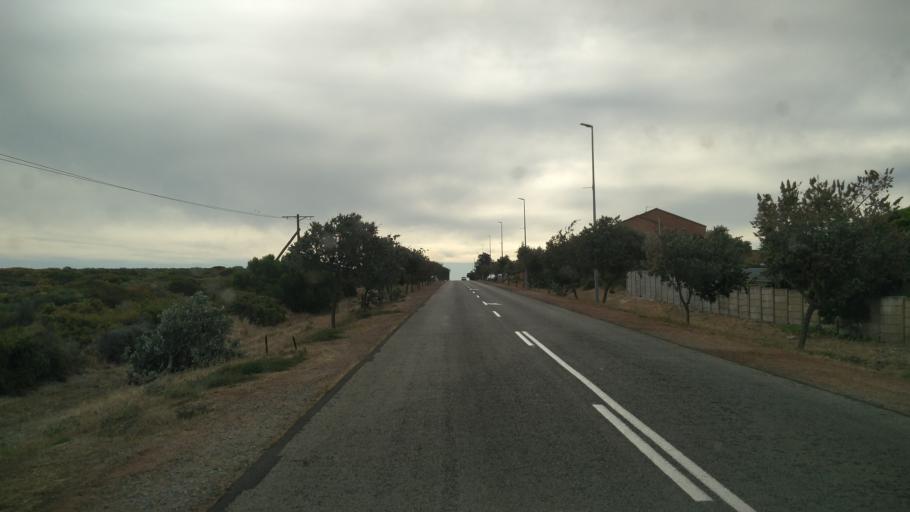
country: ZA
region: Western Cape
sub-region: City of Cape Town
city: Atlantis
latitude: -33.3436
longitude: 18.1675
